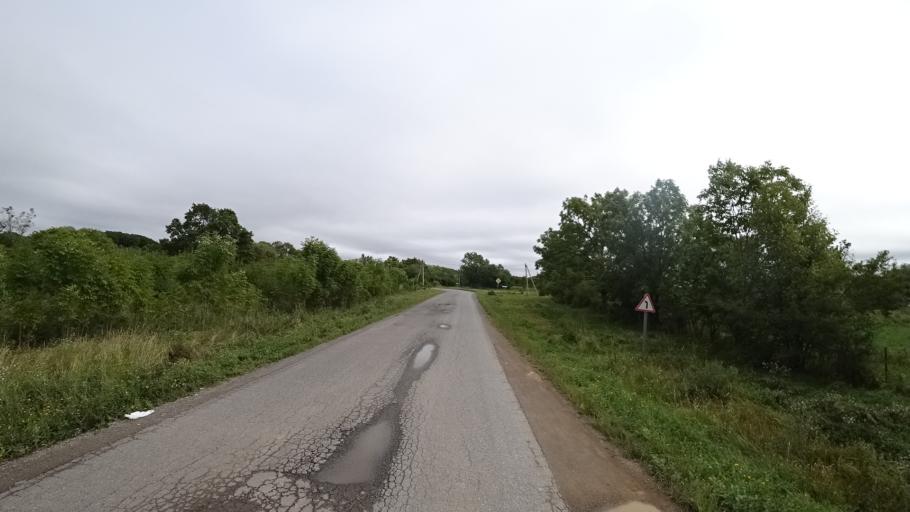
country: RU
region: Primorskiy
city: Lyalichi
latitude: 44.0739
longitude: 132.4633
